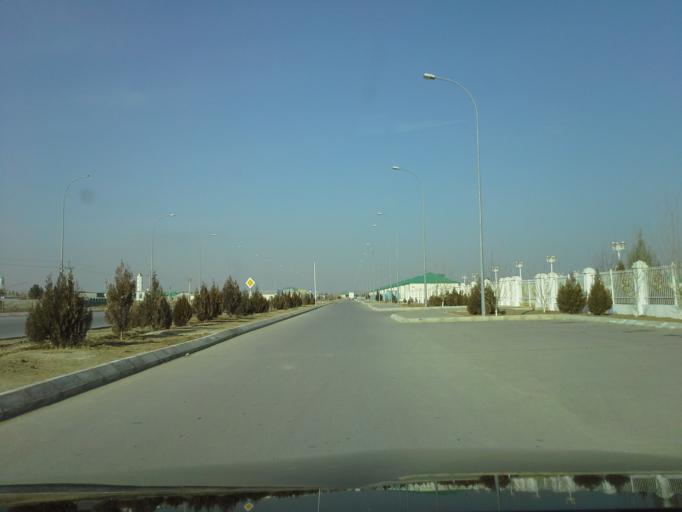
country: TM
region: Ahal
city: Abadan
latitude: 38.1703
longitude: 58.0466
